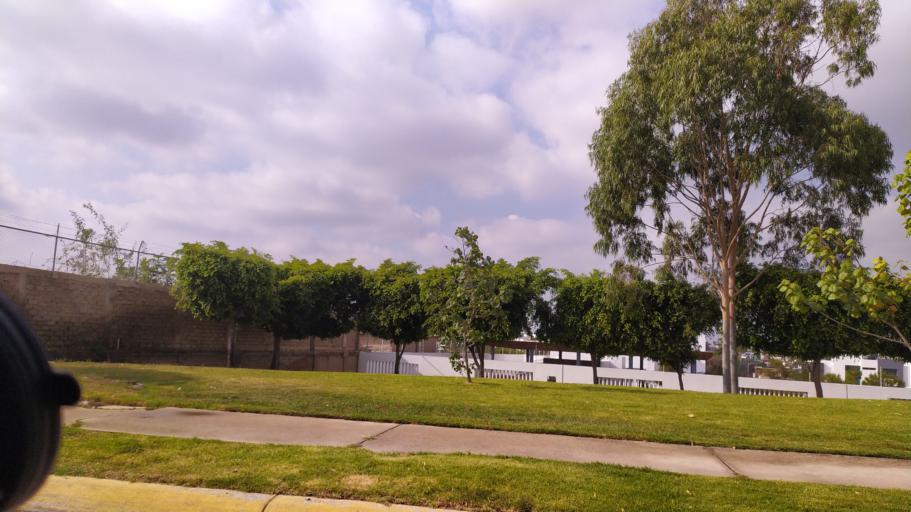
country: MX
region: Jalisco
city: Zapopan2
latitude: 20.7035
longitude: -103.4332
